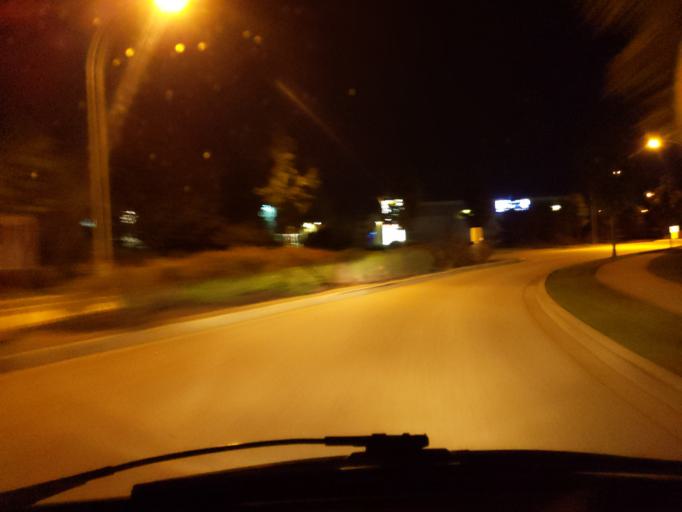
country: CA
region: British Columbia
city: Walnut Grove
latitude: 49.1786
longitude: -122.6602
